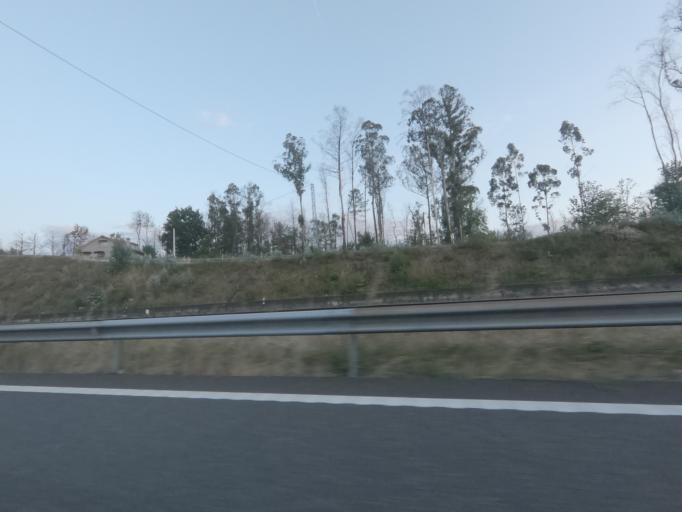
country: ES
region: Galicia
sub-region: Provincia de Pontevedra
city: Ponteareas
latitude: 42.1434
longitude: -8.4721
